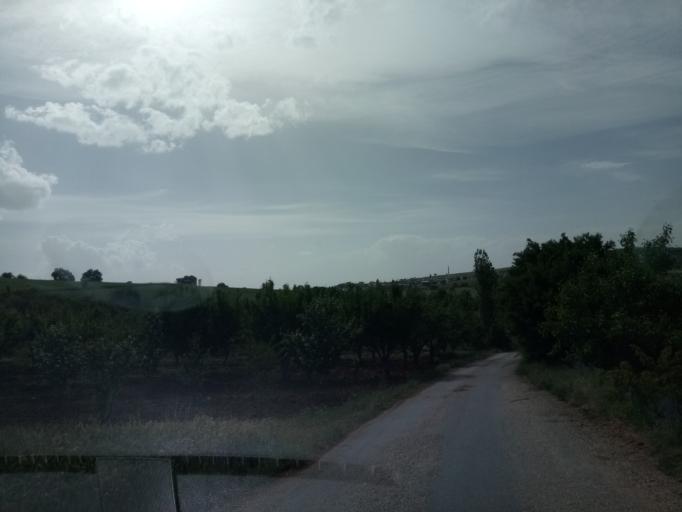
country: TR
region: Konya
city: Ahirli
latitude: 37.2820
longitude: 32.1900
